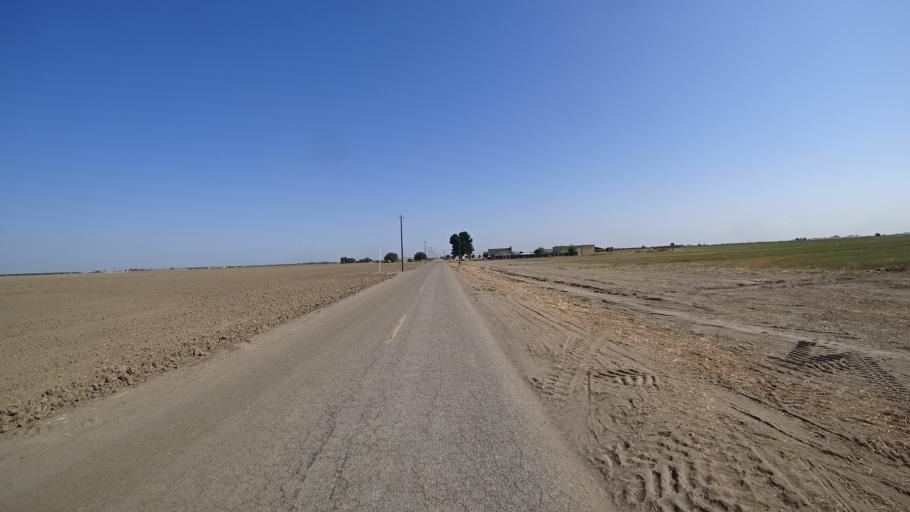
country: US
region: California
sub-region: Kings County
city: Home Garden
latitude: 36.2334
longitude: -119.5742
